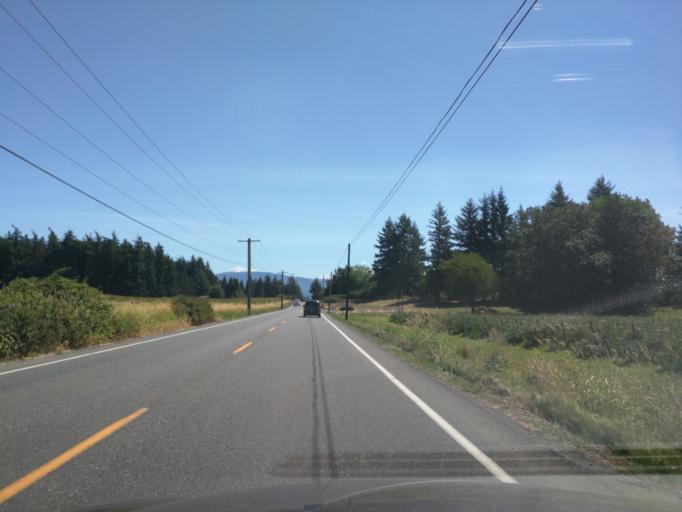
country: US
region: Washington
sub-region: Whatcom County
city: Lynden
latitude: 48.8916
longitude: -122.4624
